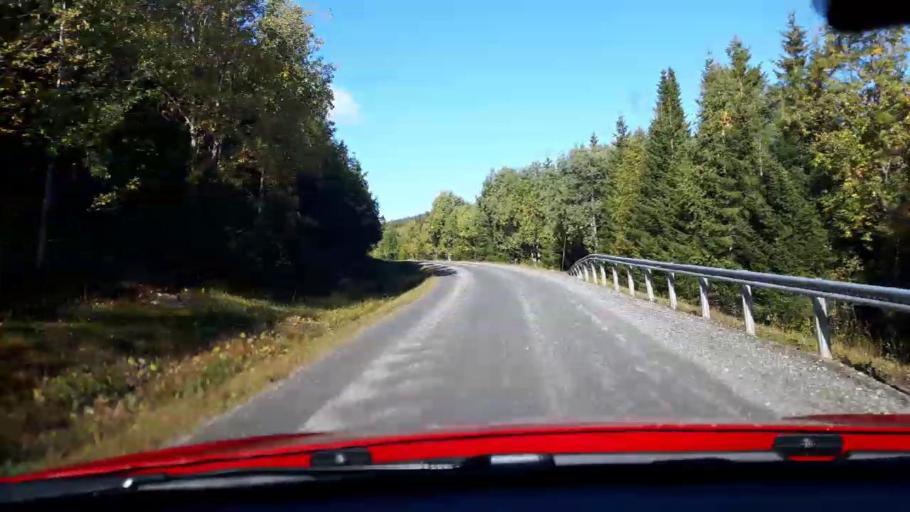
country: NO
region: Nord-Trondelag
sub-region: Lierne
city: Sandvika
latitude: 64.5851
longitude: 13.8840
